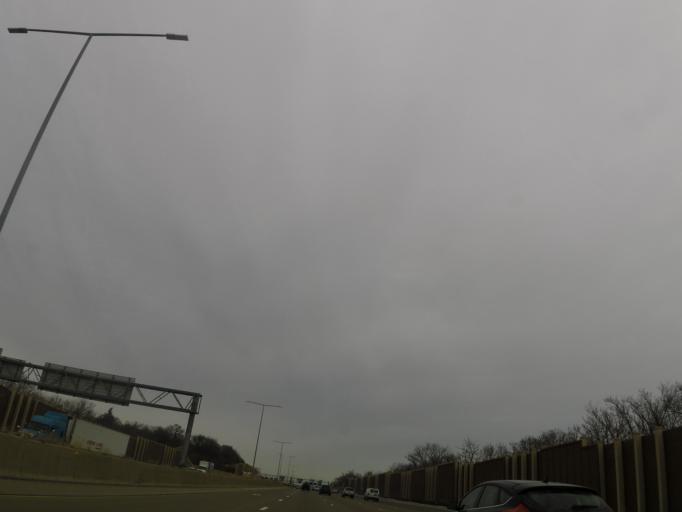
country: US
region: Minnesota
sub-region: Hennepin County
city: Richfield
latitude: 44.9067
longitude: -93.2733
